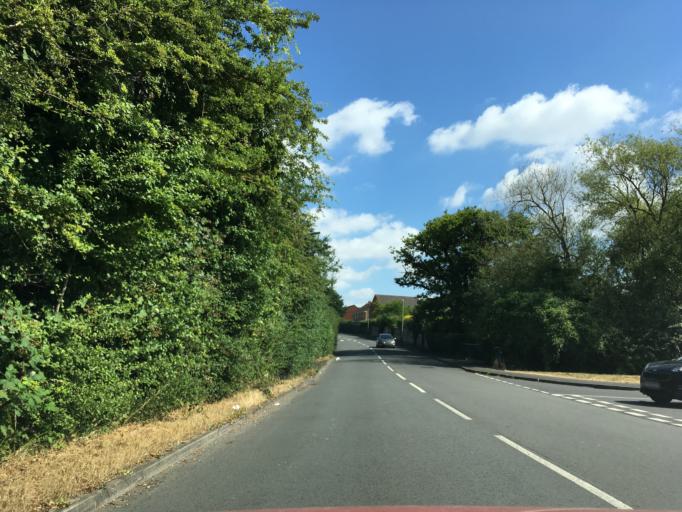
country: GB
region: England
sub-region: Gloucestershire
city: Uckington
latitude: 51.8976
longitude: -2.1311
